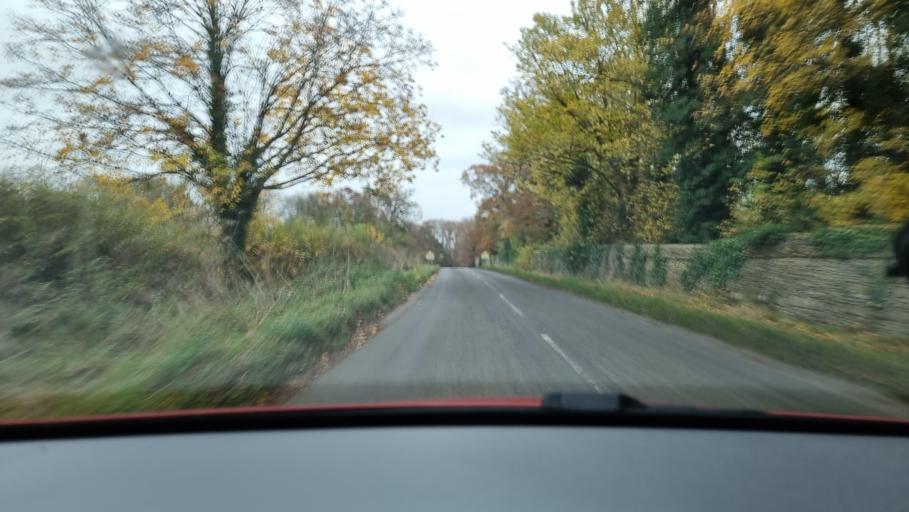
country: GB
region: England
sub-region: Oxfordshire
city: Woodstock
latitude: 51.8777
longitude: -1.3148
